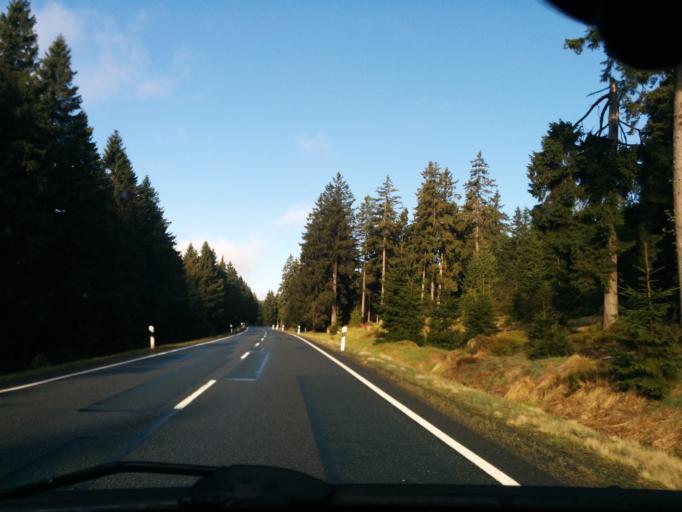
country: DE
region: Lower Saxony
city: Altenau
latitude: 51.7677
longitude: 10.4908
